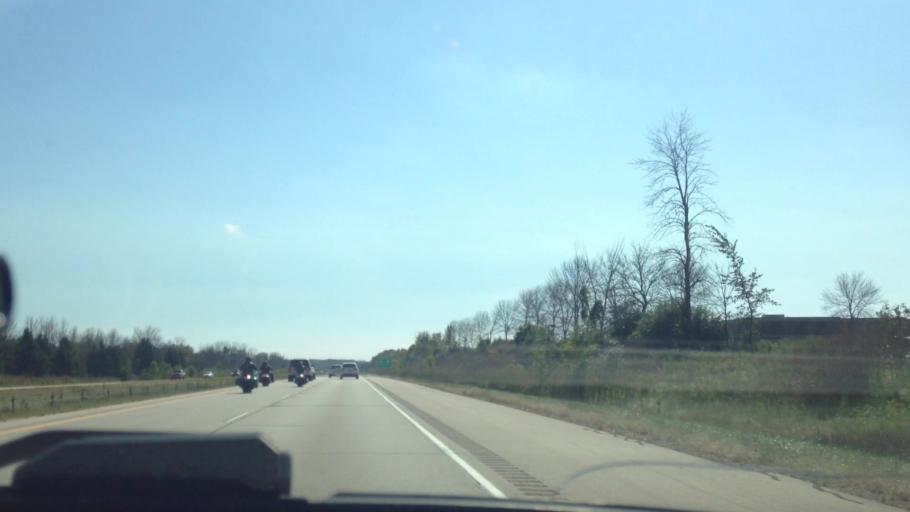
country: US
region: Wisconsin
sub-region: Ozaukee County
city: Thiensville
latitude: 43.2430
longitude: -87.9201
